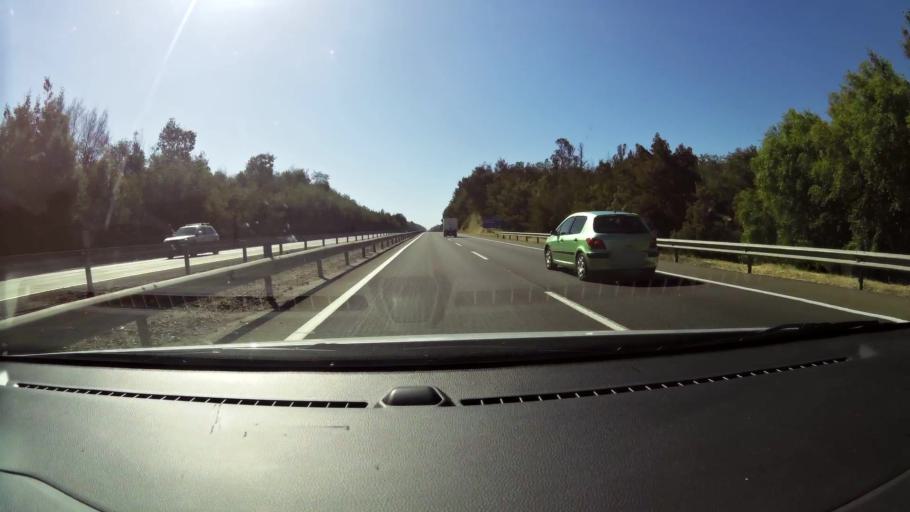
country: CL
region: Valparaiso
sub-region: Provincia de Marga Marga
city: Quilpue
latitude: -33.1779
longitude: -71.5098
